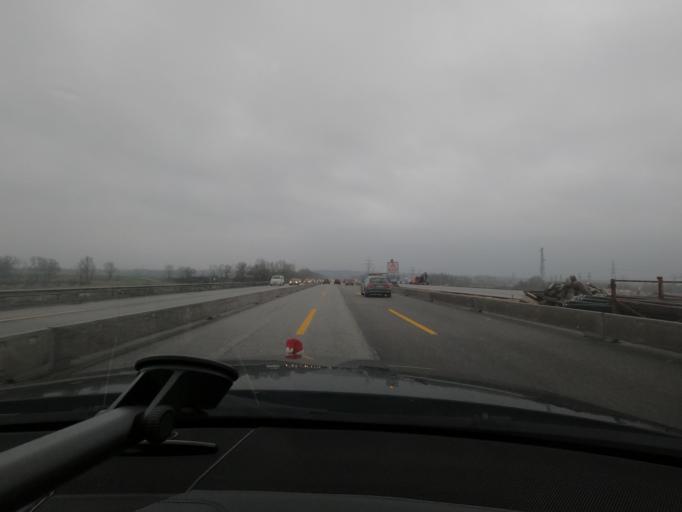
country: DE
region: Hamburg
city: Altona
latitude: 53.4952
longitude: 9.9138
